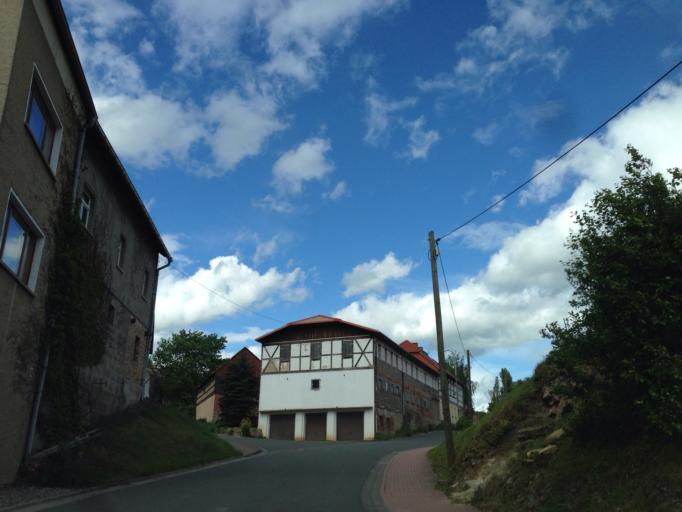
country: DE
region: Thuringia
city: Rudolstadt
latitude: 50.7753
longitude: 11.3580
